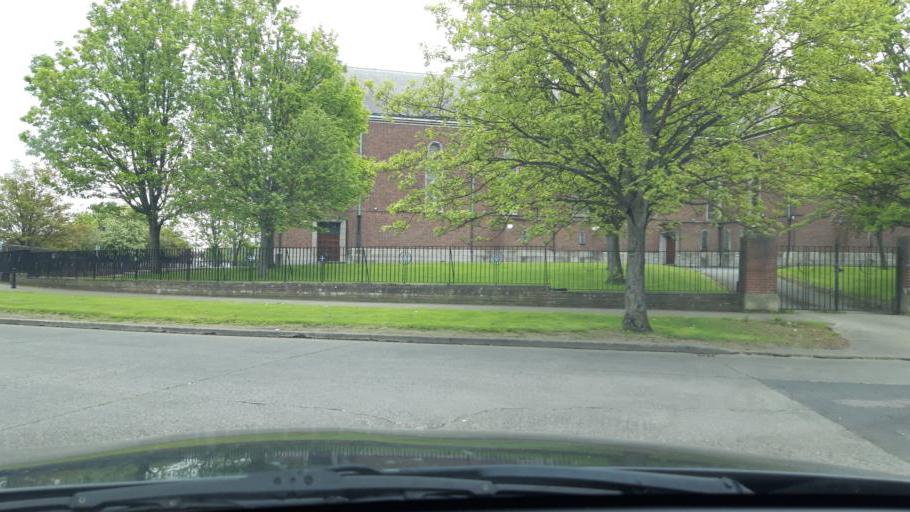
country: IE
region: Leinster
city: Crumlin
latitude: 53.3226
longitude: -6.3336
